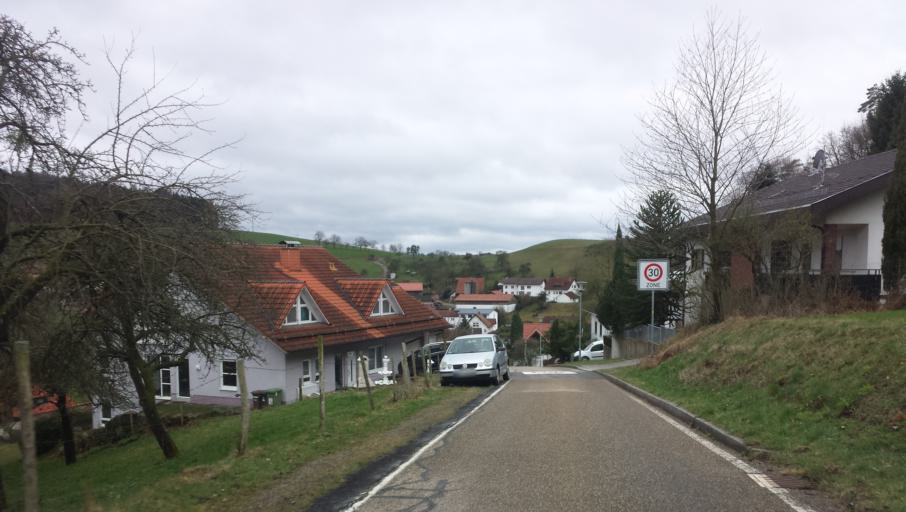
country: DE
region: Hesse
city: Unter-Abtsteinach
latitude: 49.5500
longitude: 8.7596
